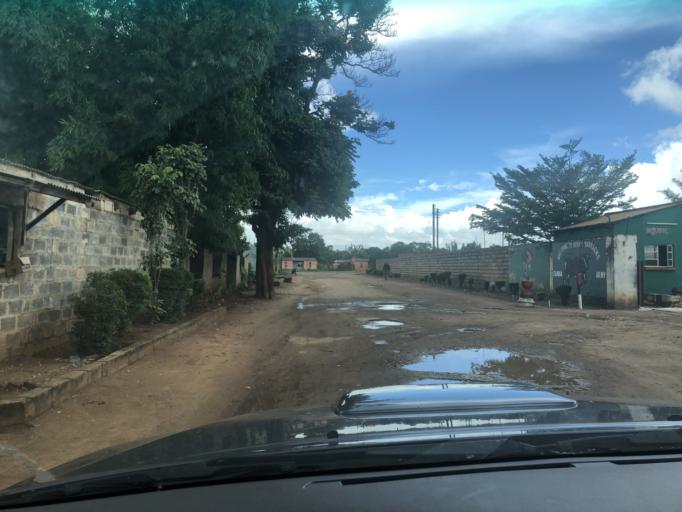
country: ZM
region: Lusaka
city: Lusaka
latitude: -15.4311
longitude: 28.3065
